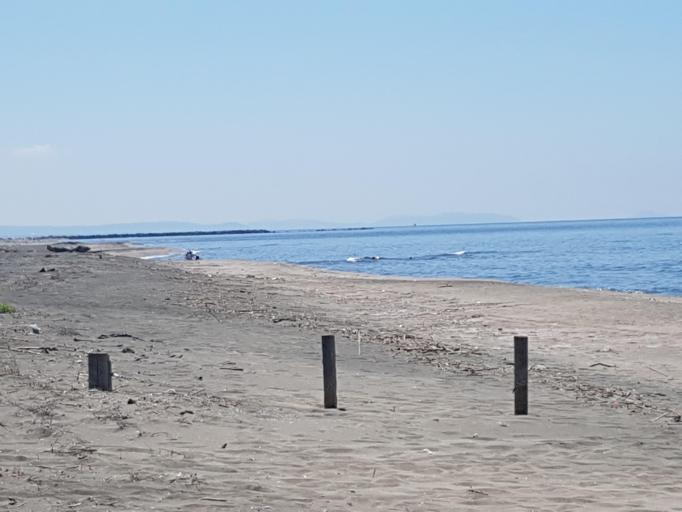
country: IT
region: Campania
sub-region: Provincia di Caserta
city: Castel Volturno
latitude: 40.9875
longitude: 13.9650
